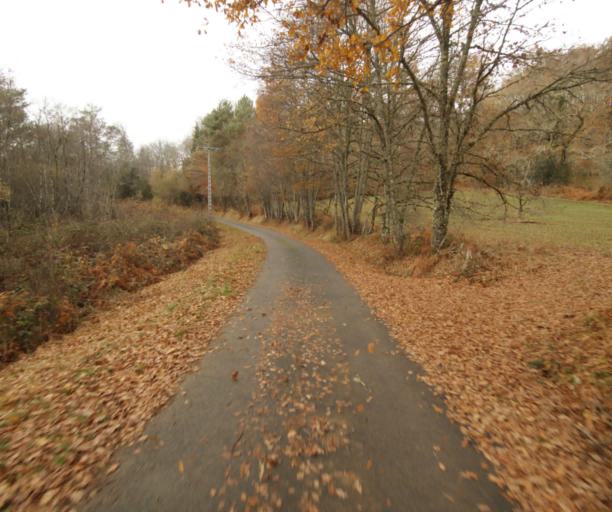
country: FR
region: Limousin
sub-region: Departement de la Correze
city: Sainte-Fortunade
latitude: 45.1782
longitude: 1.7783
